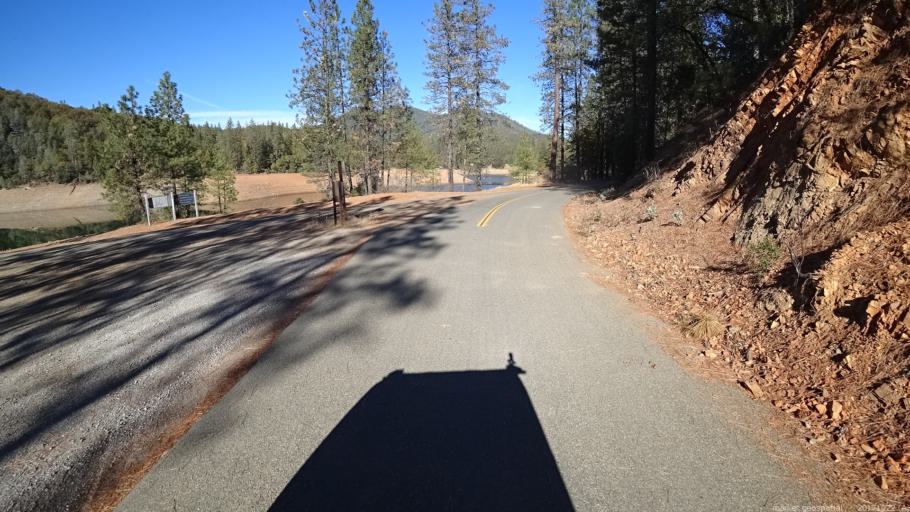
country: US
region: California
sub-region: Shasta County
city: Shasta Lake
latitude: 40.8427
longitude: -122.3526
